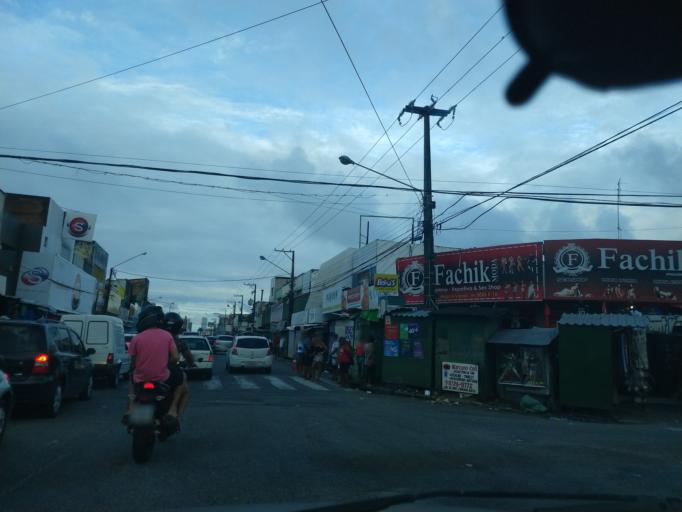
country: BR
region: Rio Grande do Norte
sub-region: Natal
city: Natal
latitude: -5.7969
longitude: -35.2177
